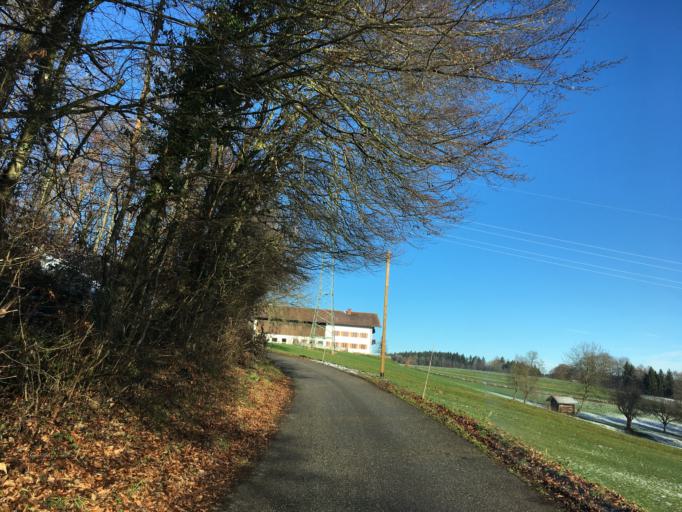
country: DE
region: Bavaria
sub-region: Upper Bavaria
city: Rimsting
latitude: 47.9123
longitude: 12.3409
